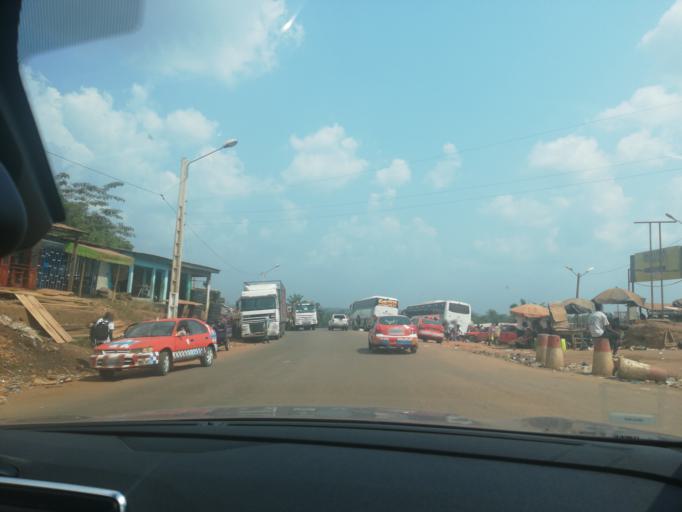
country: CI
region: Sud-Bandama
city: Divo
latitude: 5.8298
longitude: -5.3581
